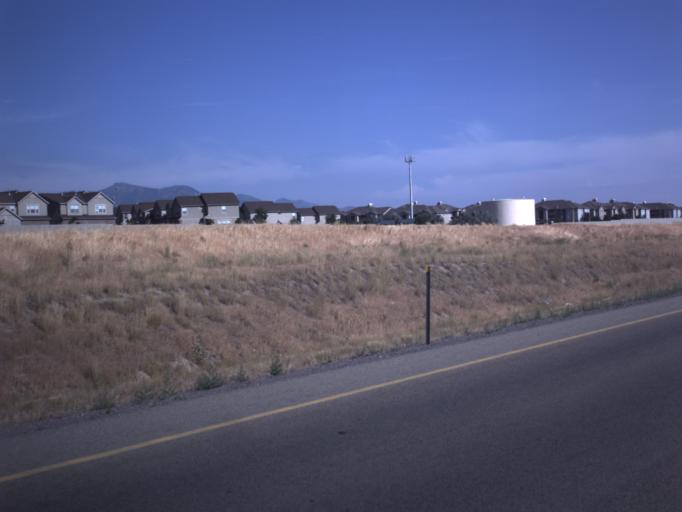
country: US
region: Utah
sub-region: Salt Lake County
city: Herriman
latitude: 40.5019
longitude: -112.0038
